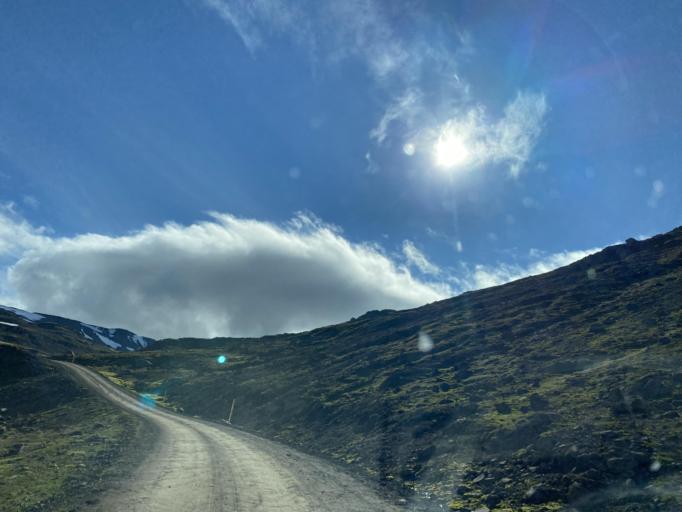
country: IS
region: East
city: Eskifjoerdur
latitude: 65.1727
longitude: -14.1184
